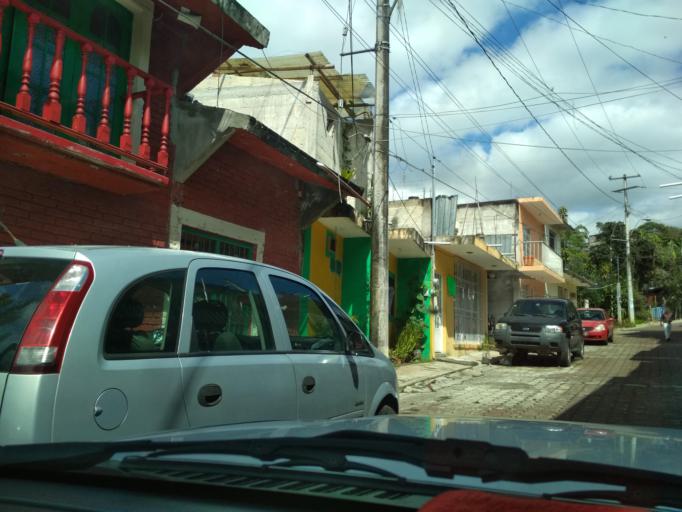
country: MX
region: Veracruz
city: Coatepec
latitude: 19.4543
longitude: -96.9367
